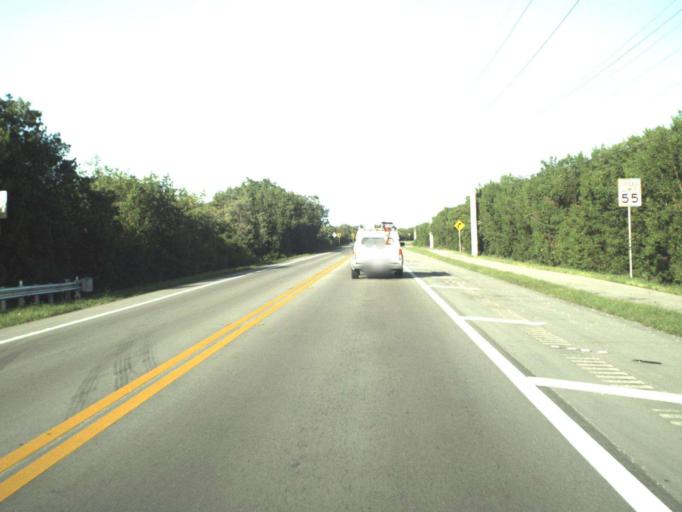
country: US
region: Florida
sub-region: Monroe County
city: Islamorada
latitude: 24.8400
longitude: -80.7916
